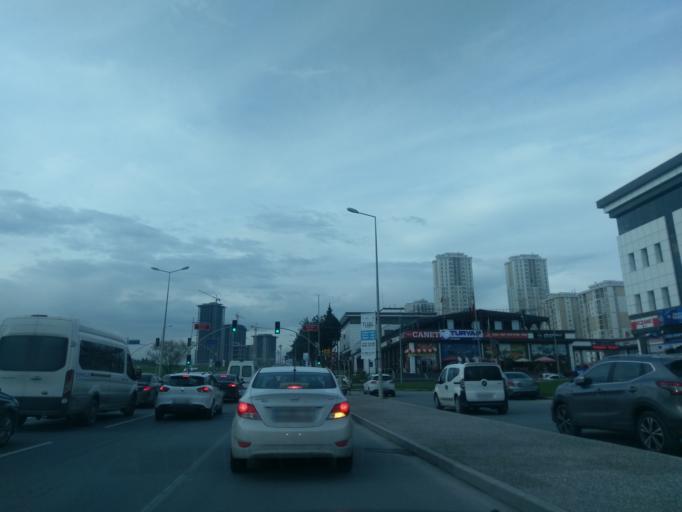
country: TR
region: Istanbul
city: Esenyurt
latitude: 41.0868
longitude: 28.6510
